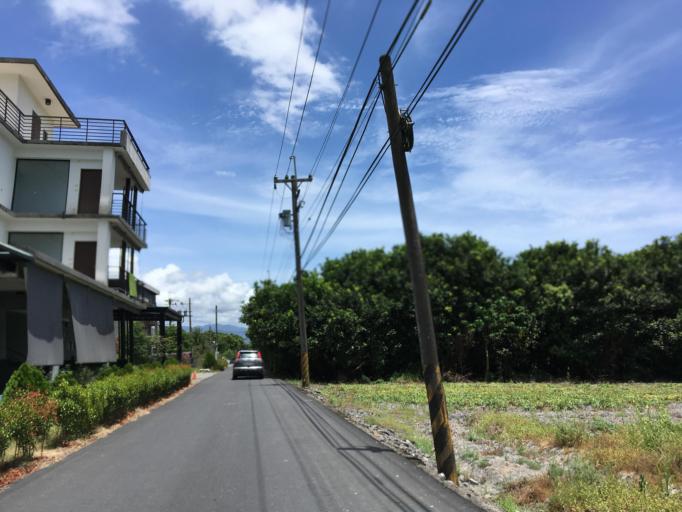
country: TW
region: Taiwan
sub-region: Yilan
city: Yilan
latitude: 24.6377
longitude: 121.7204
